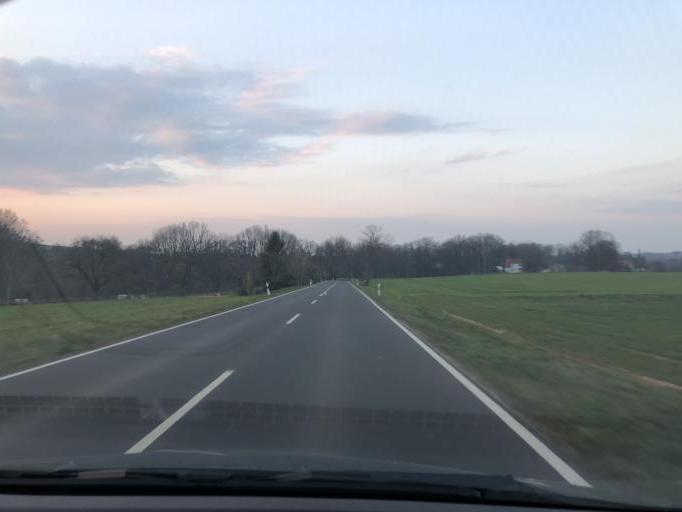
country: DE
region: Saxony
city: Elstra
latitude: 51.2300
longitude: 14.1298
